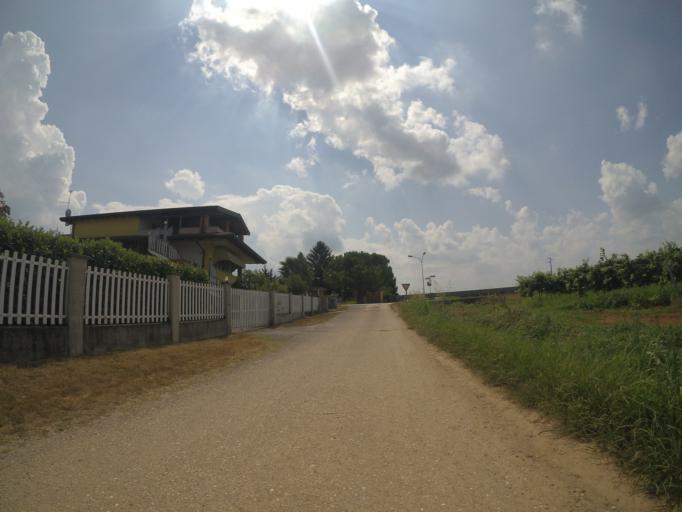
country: IT
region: Friuli Venezia Giulia
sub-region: Provincia di Udine
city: Bertiolo
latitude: 45.9513
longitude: 13.0463
